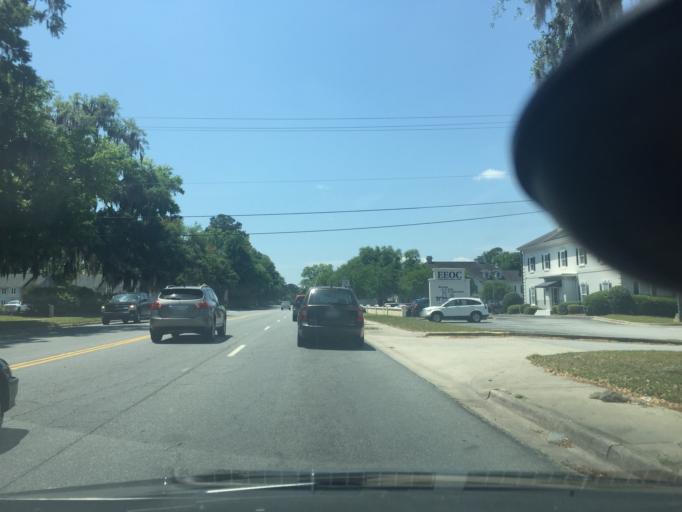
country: US
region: Georgia
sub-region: Chatham County
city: Isle of Hope
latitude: 32.0000
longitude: -81.1138
